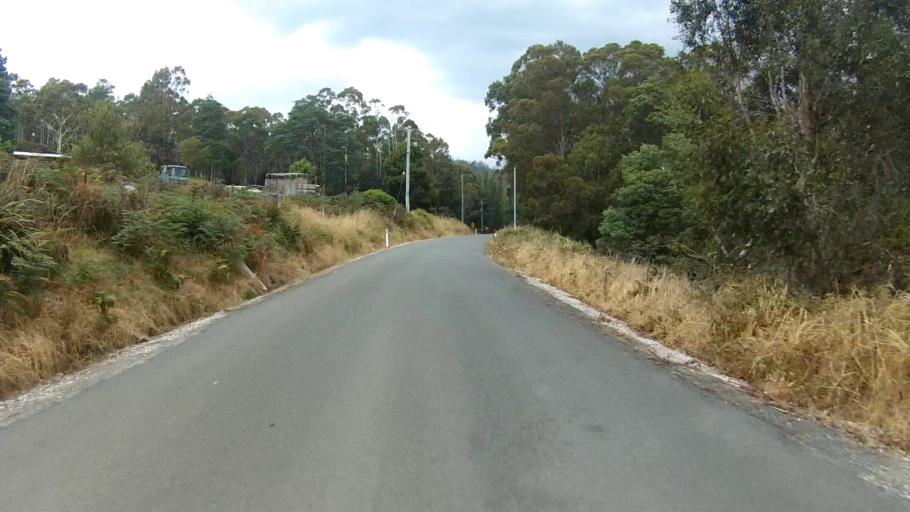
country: AU
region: Tasmania
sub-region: Huon Valley
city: Cygnet
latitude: -43.2347
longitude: 147.1569
